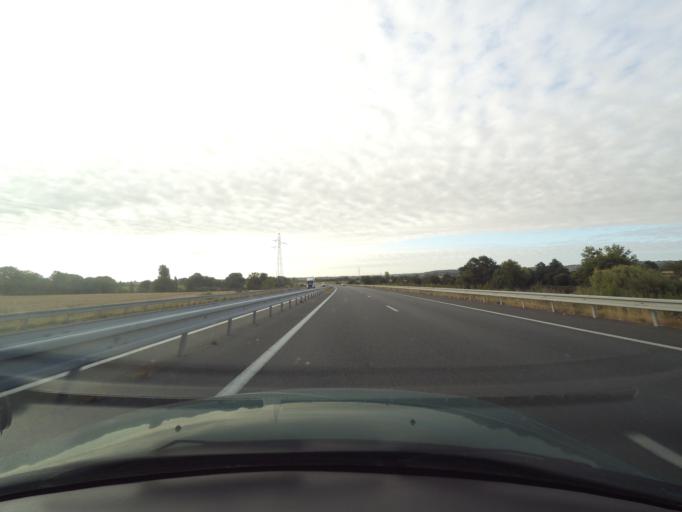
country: FR
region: Pays de la Loire
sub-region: Departement de Maine-et-Loire
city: La Tessoualle
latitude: 46.9752
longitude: -0.8130
